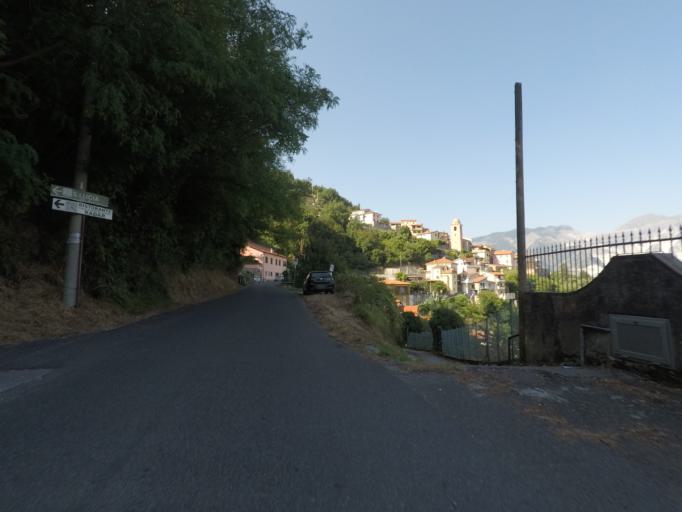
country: IT
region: Tuscany
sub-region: Provincia di Massa-Carrara
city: Carrara
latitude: 44.0742
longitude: 10.0644
